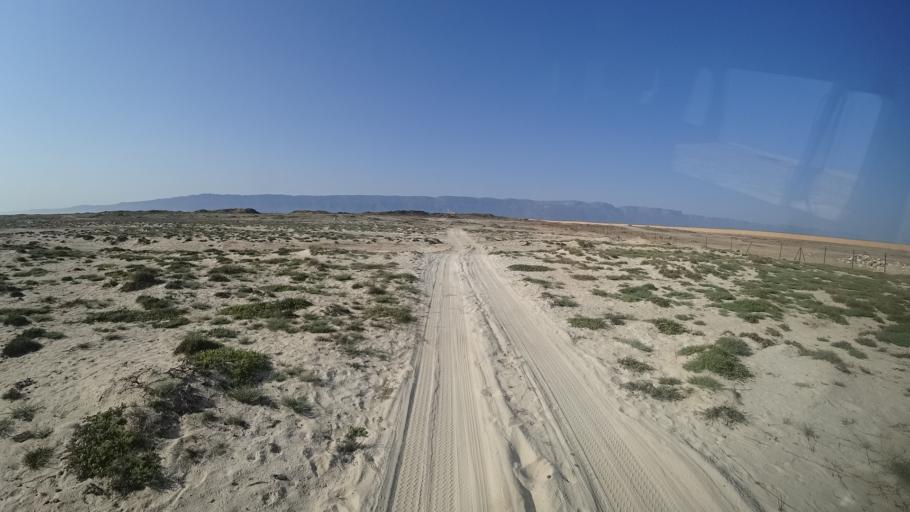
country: OM
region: Zufar
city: Salalah
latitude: 16.9444
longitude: 54.7997
